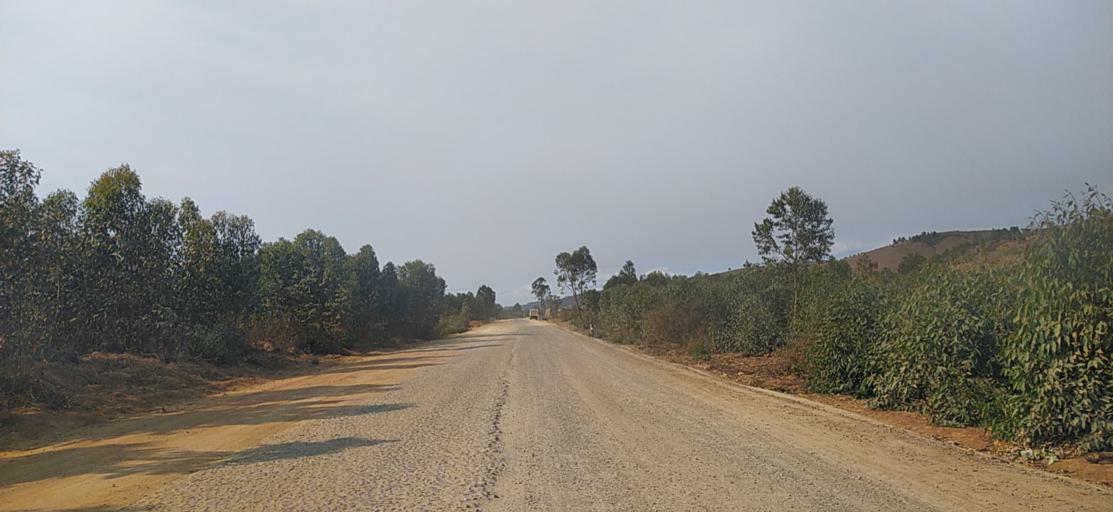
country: MG
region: Alaotra Mangoro
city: Moramanga
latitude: -18.6723
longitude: 48.2735
